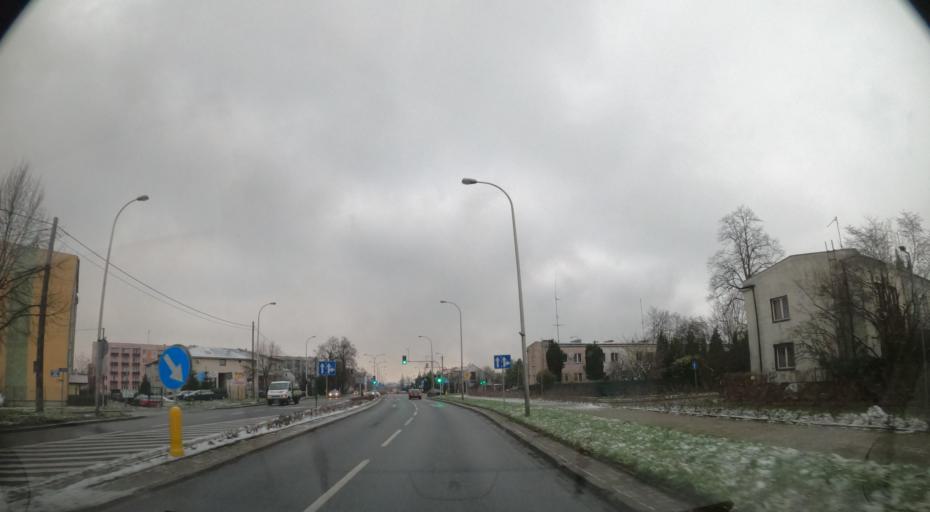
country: PL
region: Masovian Voivodeship
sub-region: Plock
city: Plock
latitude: 52.5542
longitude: 19.6713
